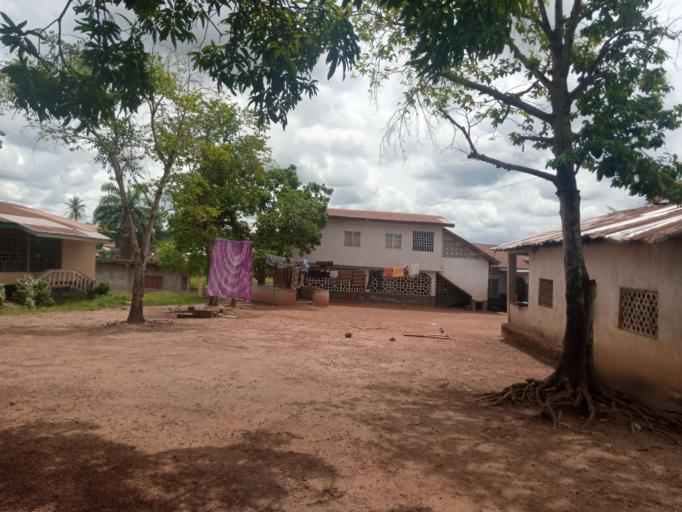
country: SL
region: Southern Province
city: Bo
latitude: 7.9549
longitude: -11.7192
